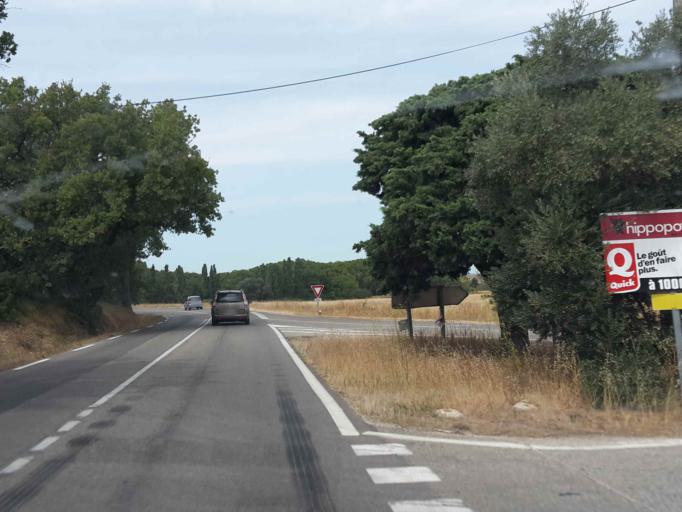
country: FR
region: Provence-Alpes-Cote d'Azur
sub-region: Departement des Bouches-du-Rhone
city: La Fare-les-Oliviers
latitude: 43.5881
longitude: 5.1772
